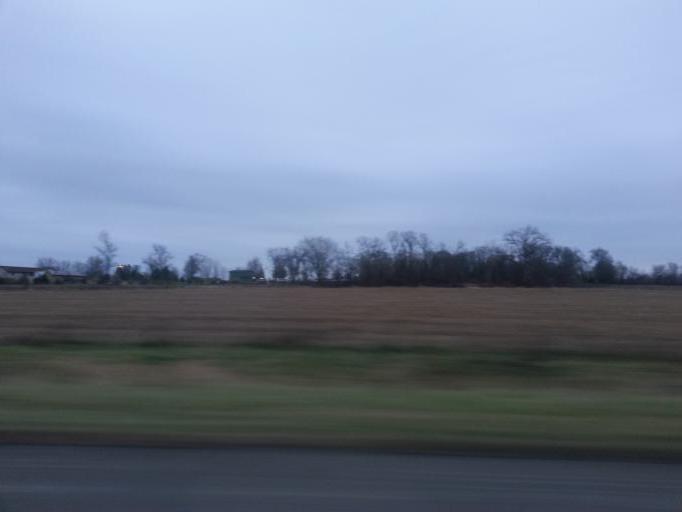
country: US
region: Iowa
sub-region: Linn County
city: Center Point
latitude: 42.1451
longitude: -91.7429
